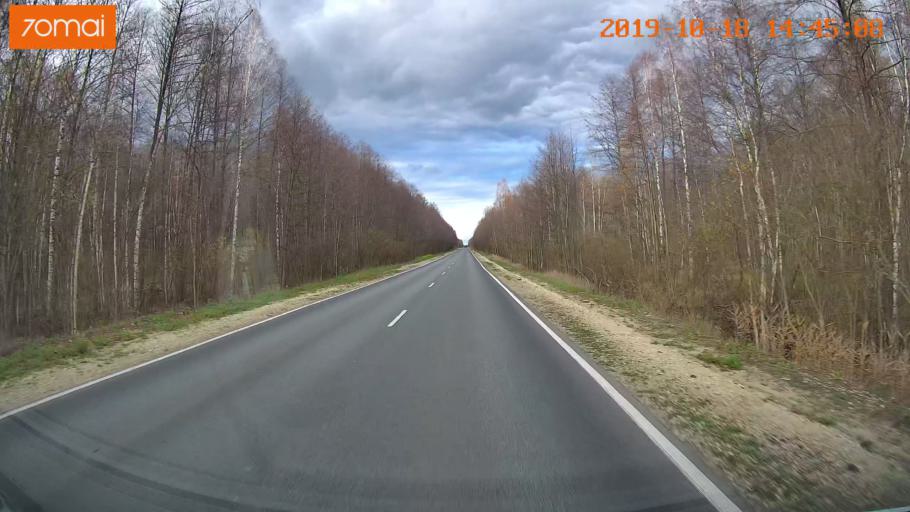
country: RU
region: Vladimir
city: Velikodvorskiy
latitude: 55.3500
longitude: 40.6783
